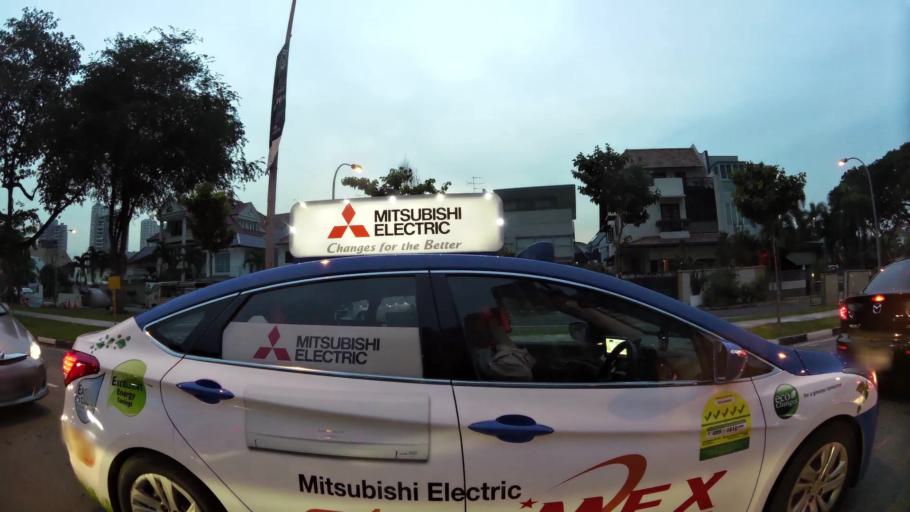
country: SG
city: Singapore
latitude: 1.3013
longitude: 103.8973
